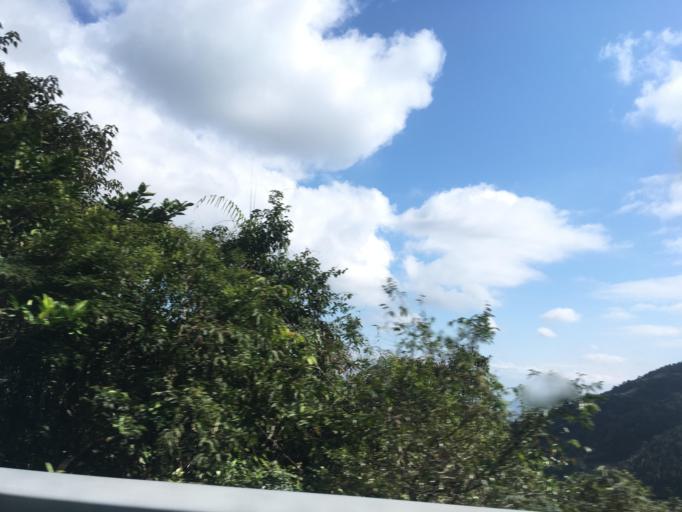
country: TW
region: Taiwan
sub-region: Yilan
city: Yilan
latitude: 24.7519
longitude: 121.6422
